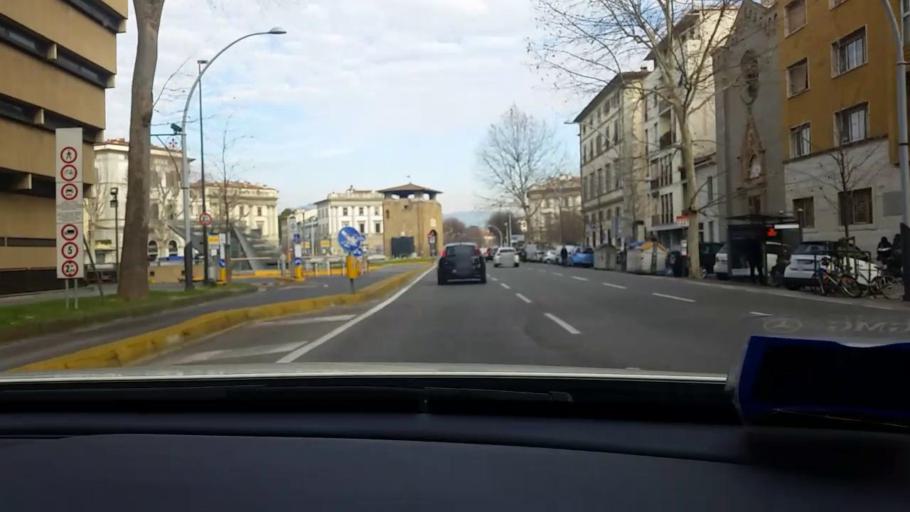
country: IT
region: Tuscany
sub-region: Province of Florence
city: Florence
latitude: 43.7692
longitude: 11.2711
